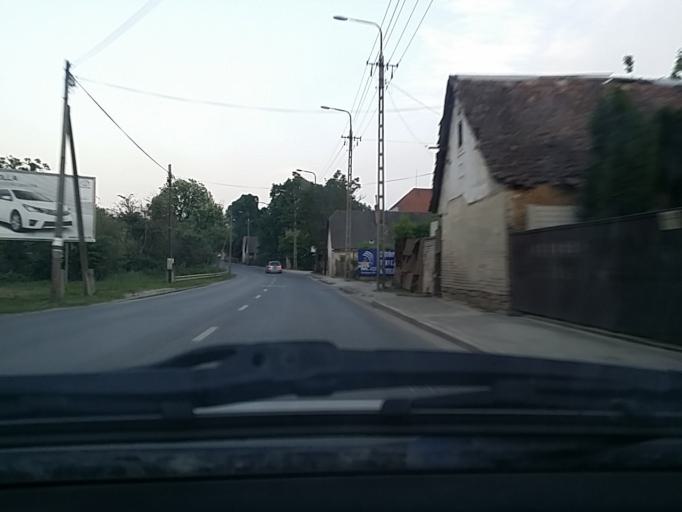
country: HU
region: Pest
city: Solymar
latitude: 47.5659
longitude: 18.9567
